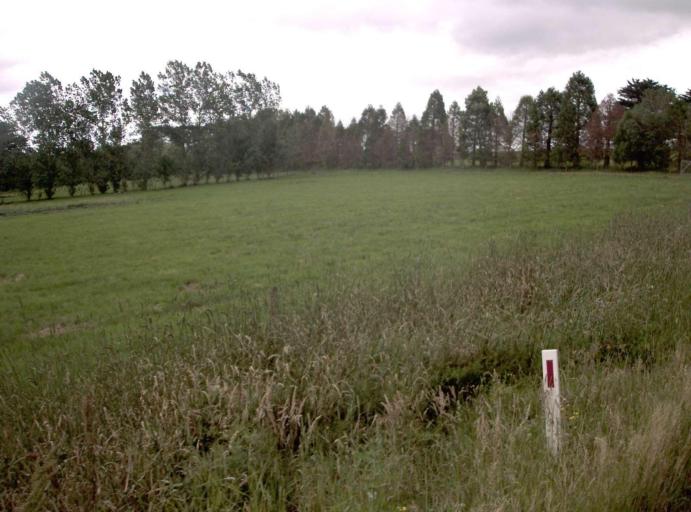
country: AU
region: Victoria
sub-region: Baw Baw
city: Warragul
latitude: -38.1107
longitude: 145.9763
